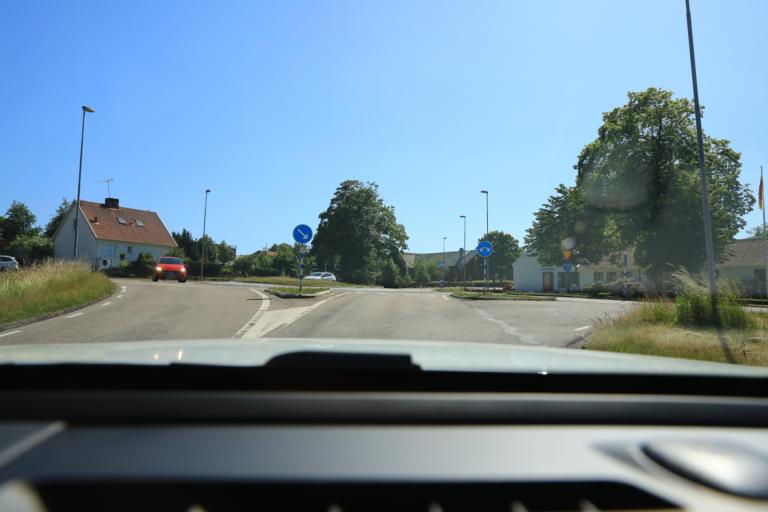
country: SE
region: Halland
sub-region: Varbergs Kommun
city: Varberg
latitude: 57.1600
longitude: 12.3133
